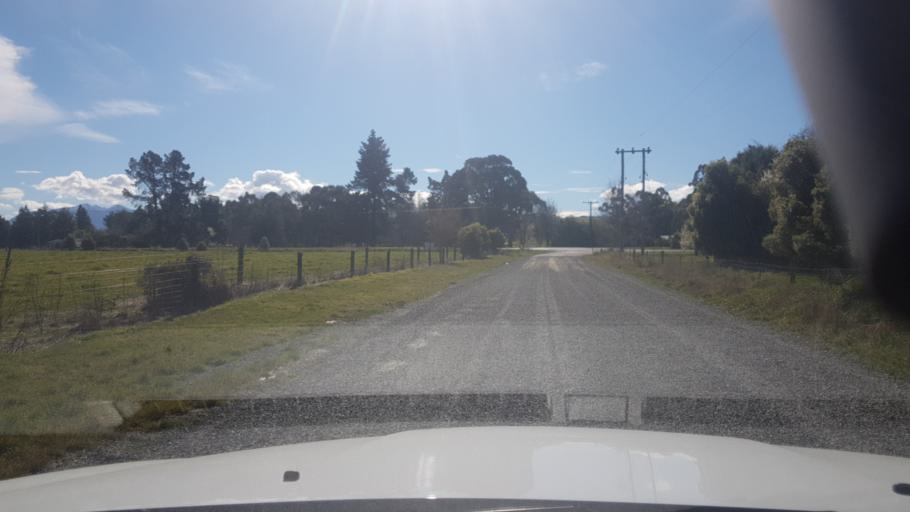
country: NZ
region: Canterbury
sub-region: Timaru District
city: Pleasant Point
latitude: -44.1138
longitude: 171.2247
